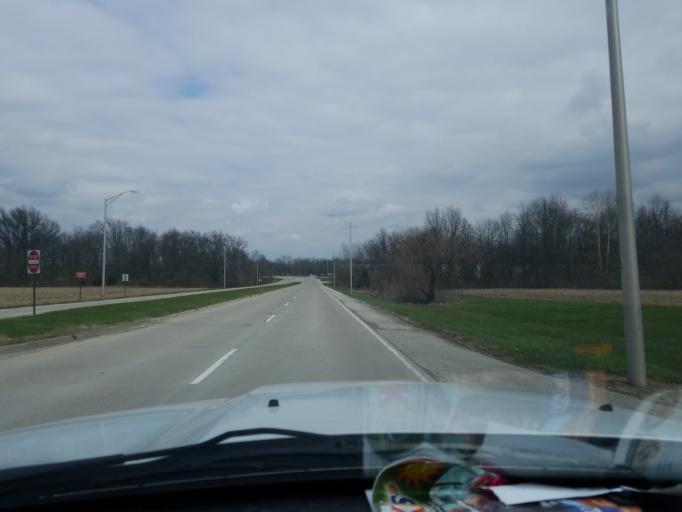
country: US
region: Indiana
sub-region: Sullivan County
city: Farmersburg
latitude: 39.3426
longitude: -87.3954
